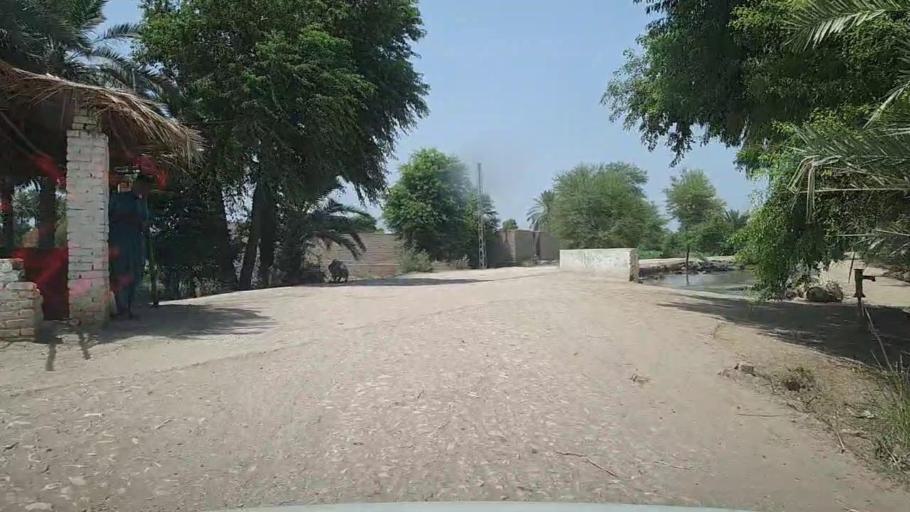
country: PK
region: Sindh
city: Pano Aqil
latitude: 27.8550
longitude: 69.1337
